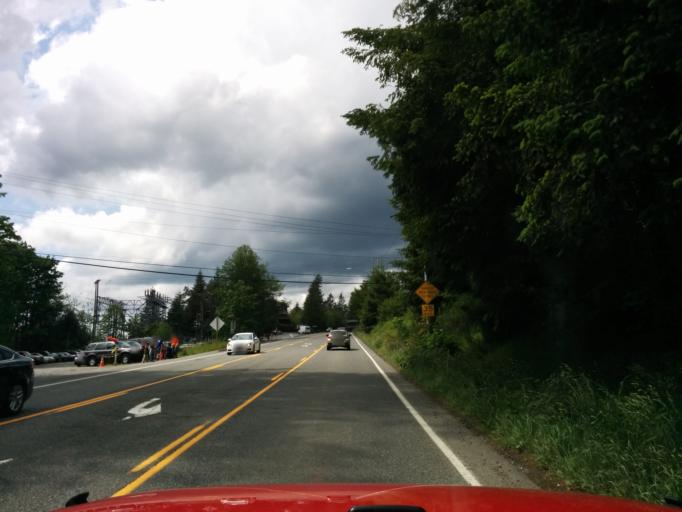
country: US
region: Washington
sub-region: King County
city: Snoqualmie
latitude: 47.5405
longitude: -121.8337
